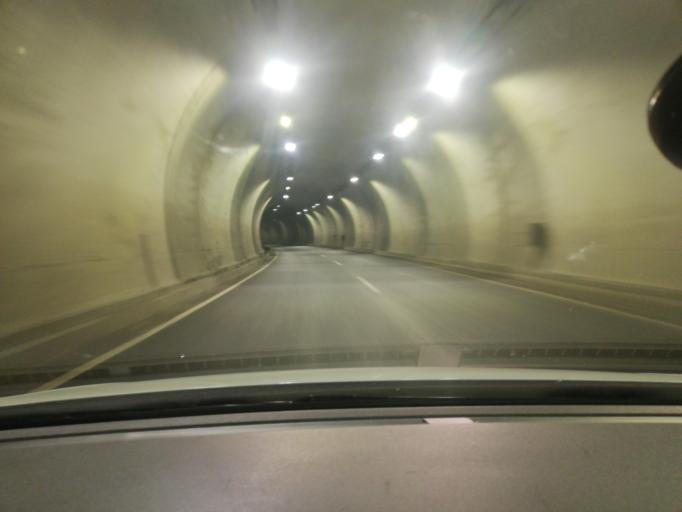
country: TR
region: Zonguldak
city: Kozlu
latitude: 41.4226
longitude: 31.7234
